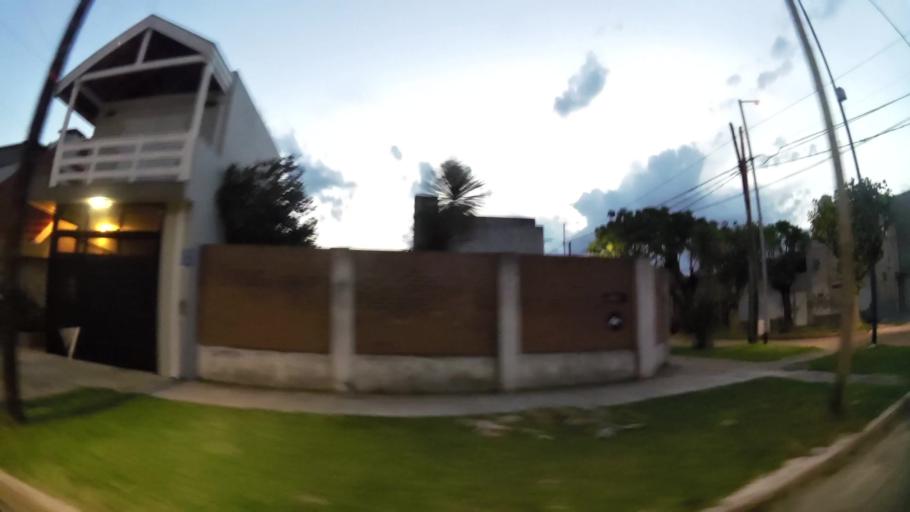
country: AR
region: Buenos Aires
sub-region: Partido de Quilmes
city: Quilmes
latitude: -34.6960
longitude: -58.3102
